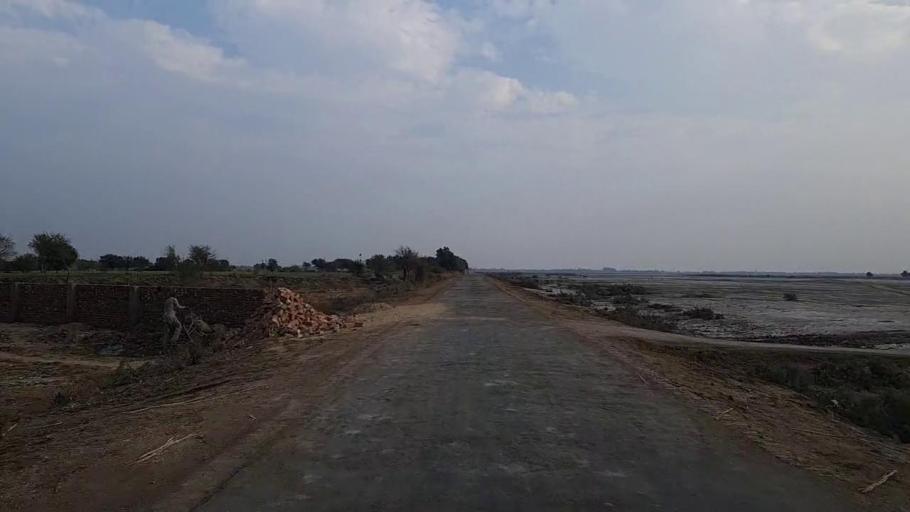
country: PK
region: Sindh
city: Pithoro
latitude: 25.4799
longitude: 69.2654
